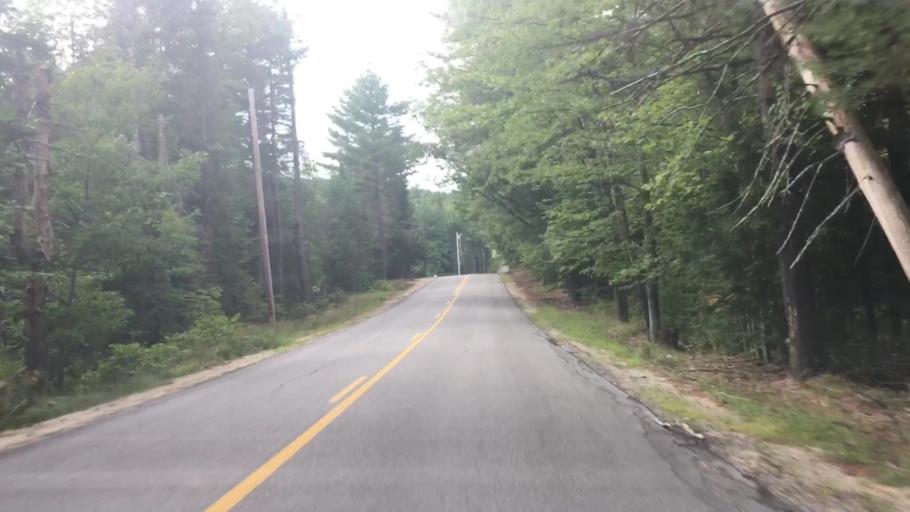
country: US
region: Maine
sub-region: Oxford County
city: Oxford
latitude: 44.0587
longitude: -70.5597
